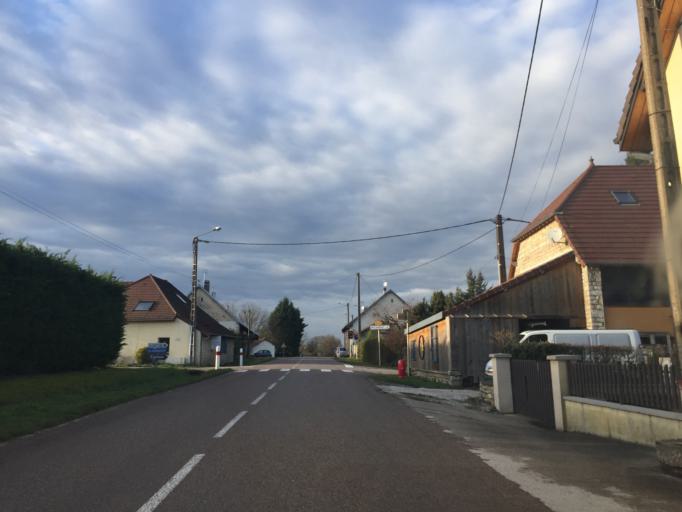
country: FR
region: Franche-Comte
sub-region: Departement du Jura
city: Mont-sous-Vaudrey
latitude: 46.9315
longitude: 5.6781
